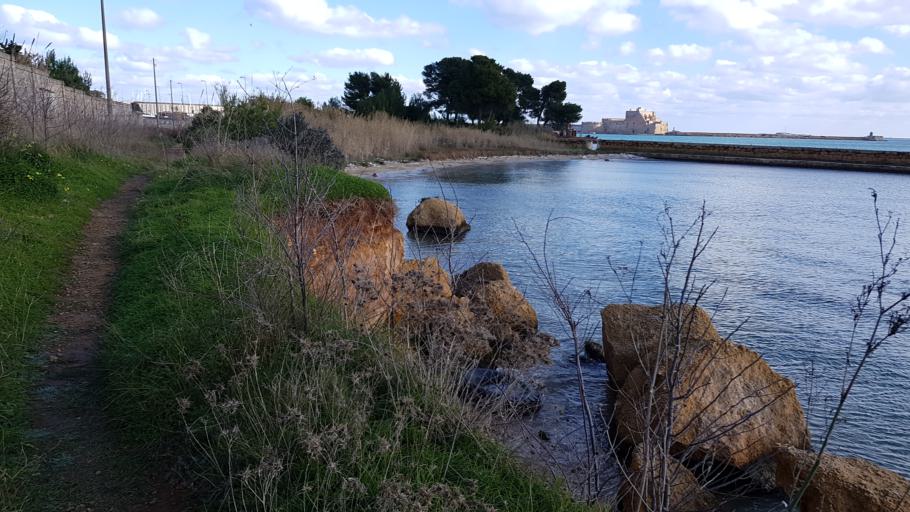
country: IT
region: Apulia
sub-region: Provincia di Brindisi
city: Materdomini
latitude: 40.6538
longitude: 17.9567
